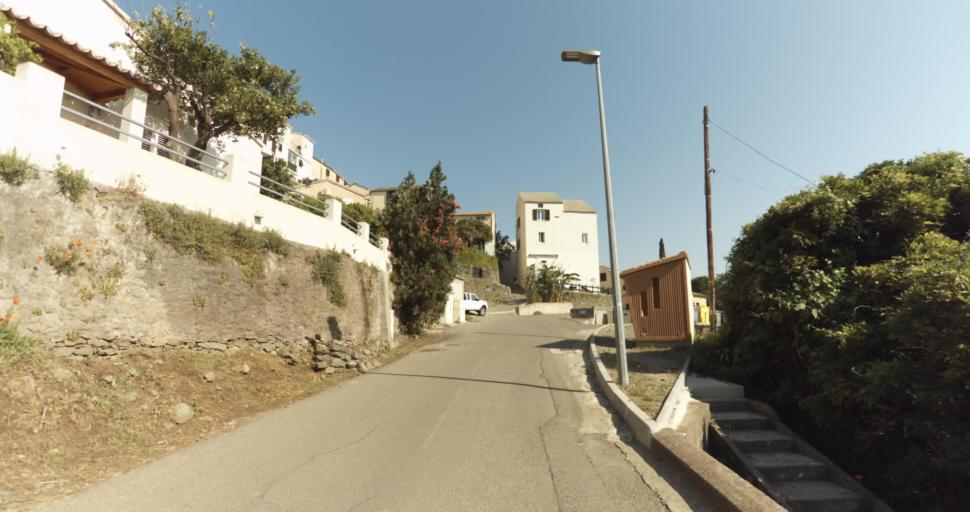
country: FR
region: Corsica
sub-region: Departement de la Haute-Corse
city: Biguglia
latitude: 42.6267
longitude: 9.4207
